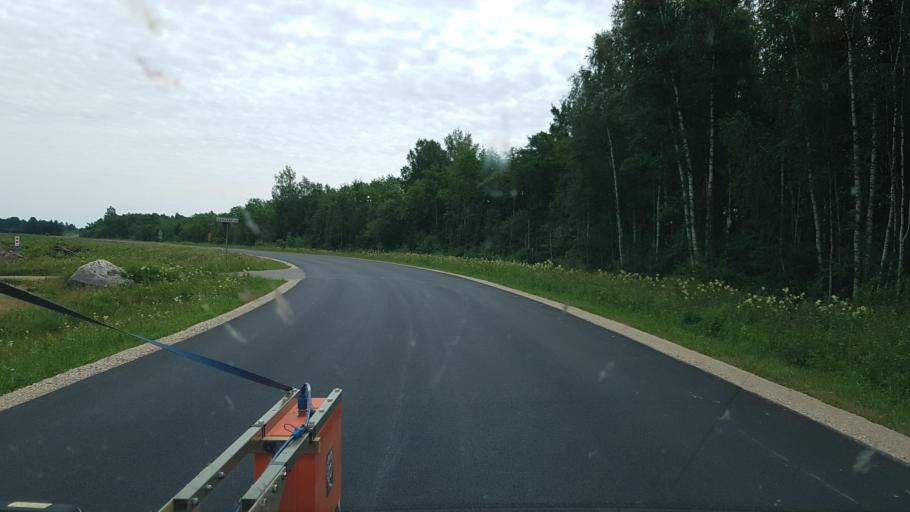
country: EE
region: Paernumaa
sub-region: Halinga vald
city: Parnu-Jaagupi
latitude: 58.6200
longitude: 24.2742
